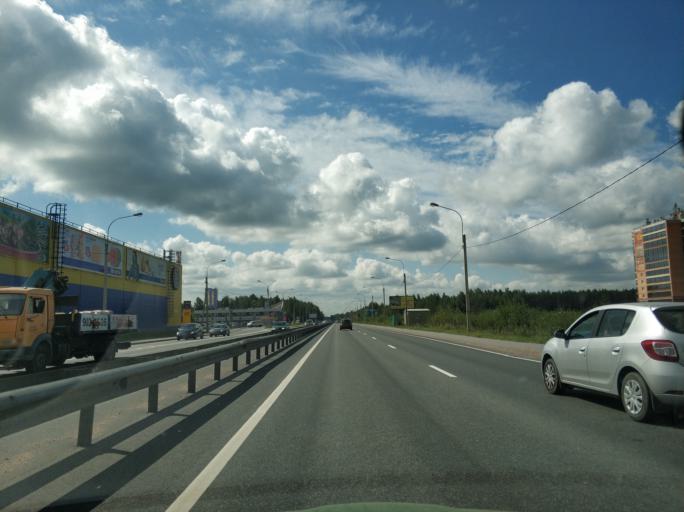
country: RU
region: Leningrad
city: Vsevolozhsk
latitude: 60.0224
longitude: 30.6055
